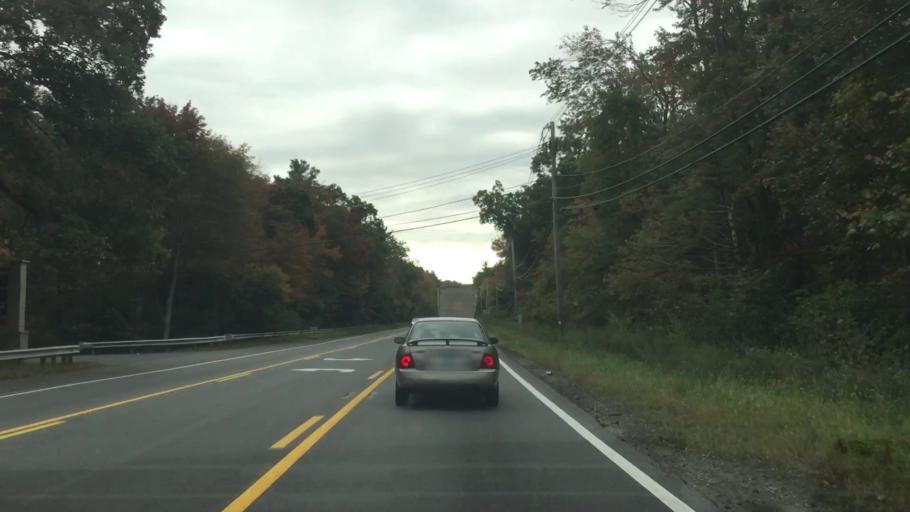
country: US
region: Massachusetts
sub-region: Middlesex County
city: North Reading
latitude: 42.6330
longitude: -71.0709
